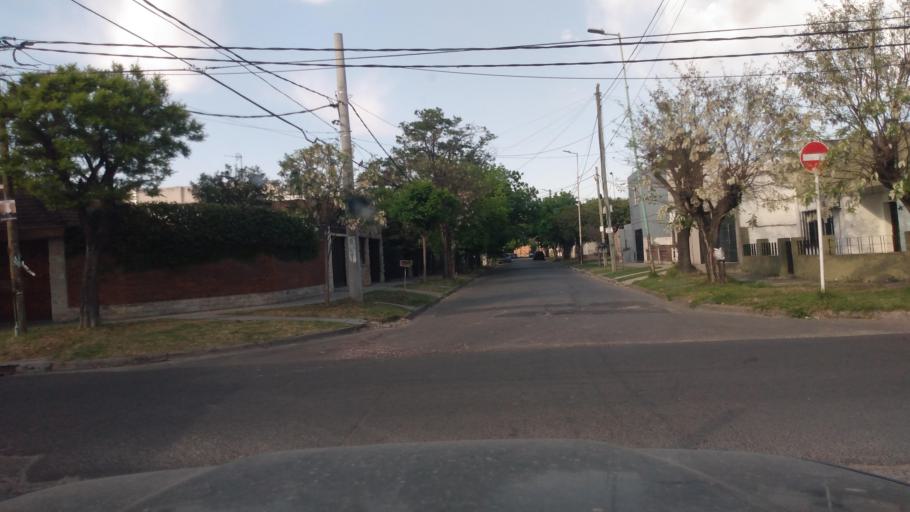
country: AR
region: Buenos Aires
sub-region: Partido de Moron
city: Moron
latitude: -34.6373
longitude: -58.6205
